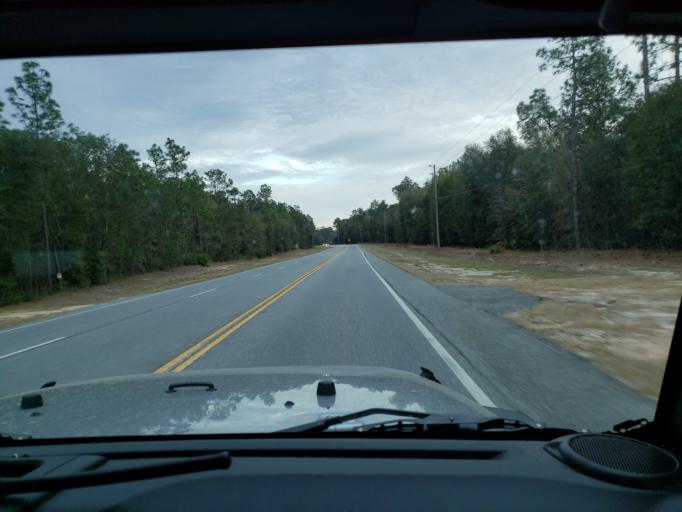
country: US
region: Georgia
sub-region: Chatham County
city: Bloomingdale
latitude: 32.0408
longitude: -81.3301
